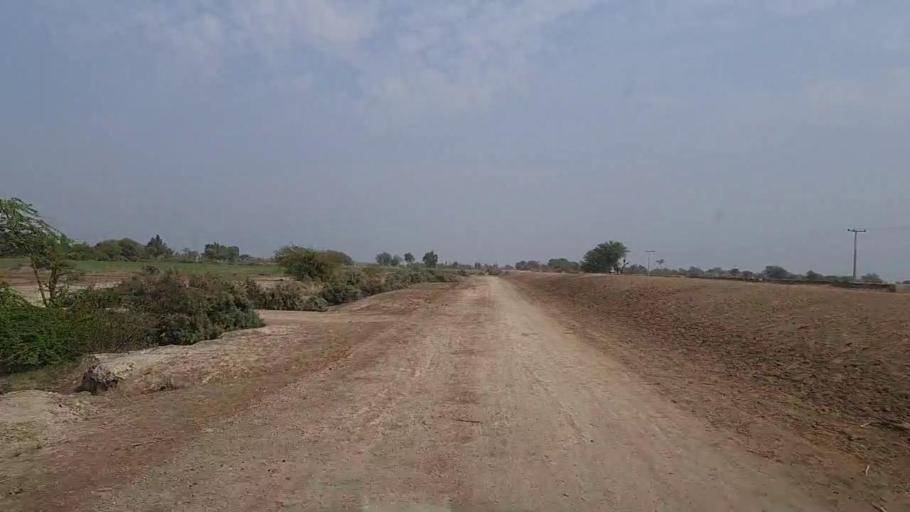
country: PK
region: Sindh
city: Mirwah Gorchani
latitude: 25.3978
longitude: 69.1030
